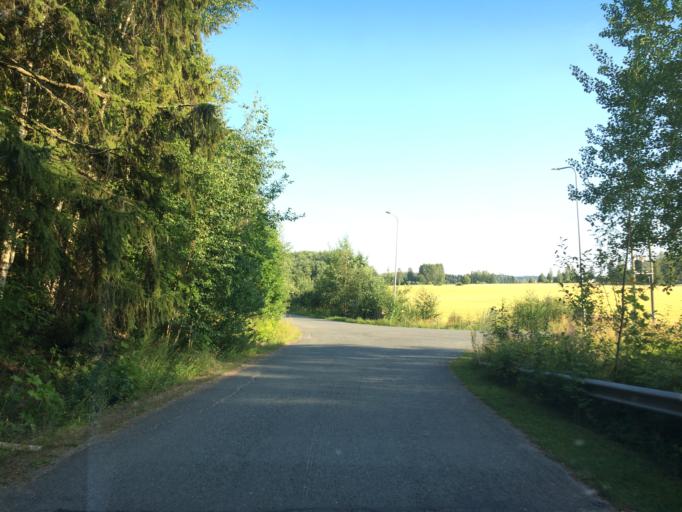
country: FI
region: Haeme
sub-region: Haemeenlinna
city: Parola
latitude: 61.0380
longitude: 24.4141
